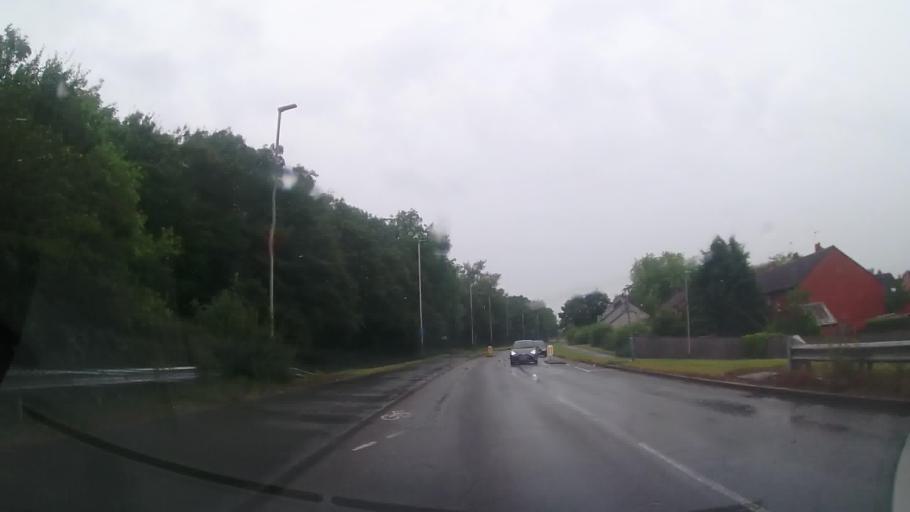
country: GB
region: England
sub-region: Leicestershire
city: Anstey
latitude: 52.6716
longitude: -1.1643
